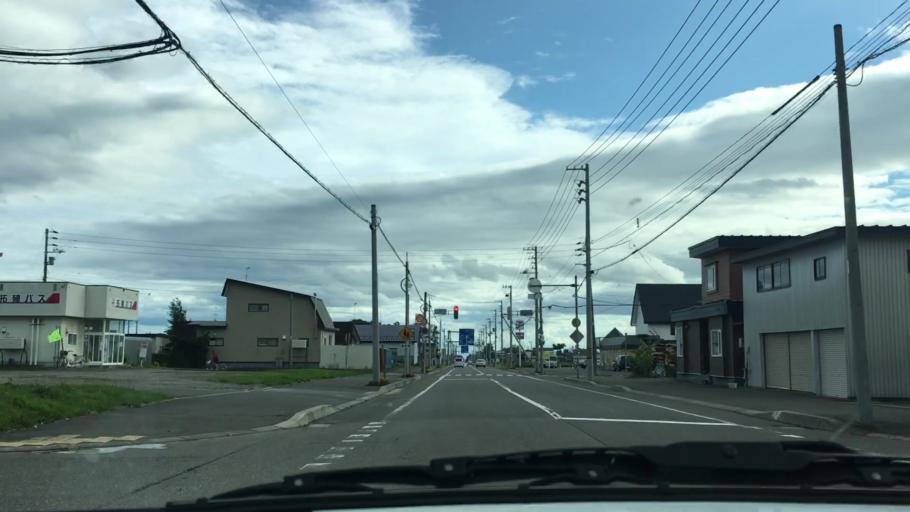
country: JP
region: Hokkaido
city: Otofuke
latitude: 43.2299
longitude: 143.2944
